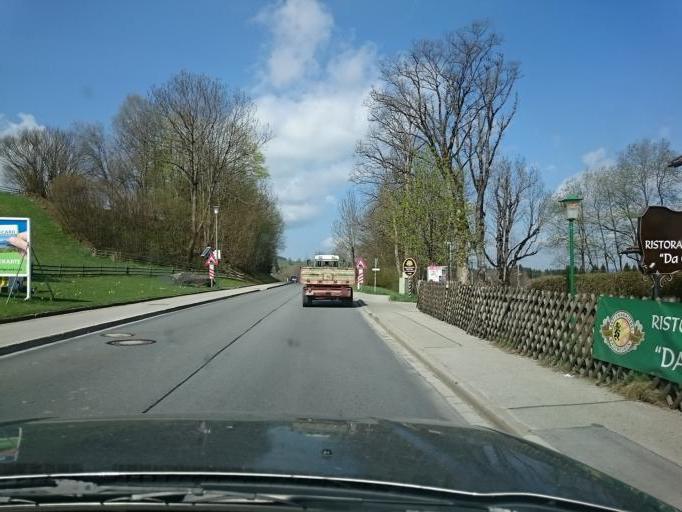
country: DE
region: Bavaria
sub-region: Upper Bavaria
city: Bad Kohlgrub
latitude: 47.6696
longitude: 11.0405
